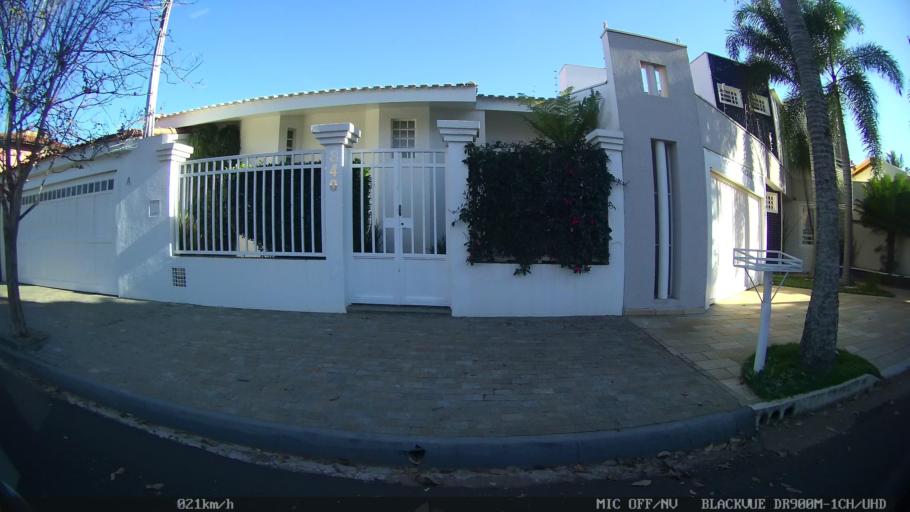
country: BR
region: Sao Paulo
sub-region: Franca
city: Franca
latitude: -20.5616
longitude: -47.4028
